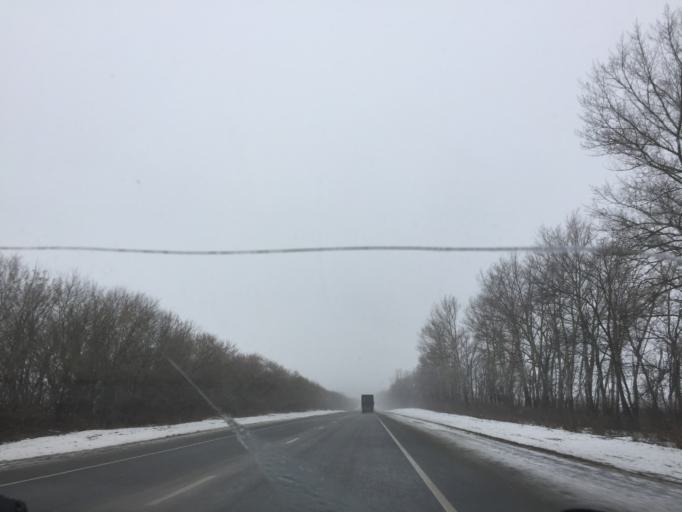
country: RU
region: Tula
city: Plavsk
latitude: 53.7702
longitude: 37.3479
